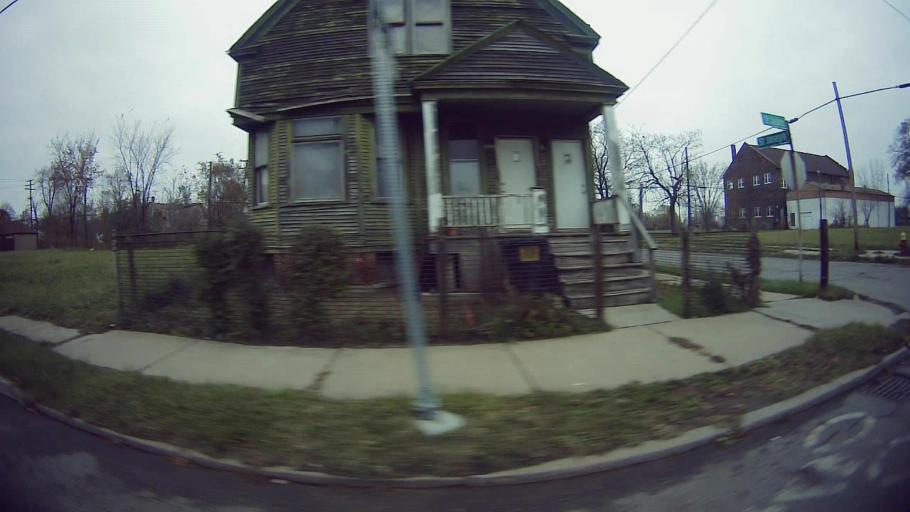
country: US
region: Michigan
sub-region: Wayne County
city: Detroit
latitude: 42.3560
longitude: -83.0387
